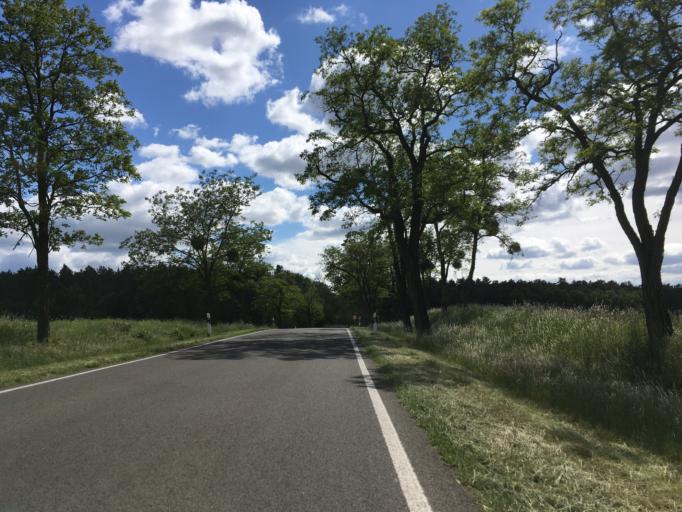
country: DE
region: Brandenburg
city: Protzel
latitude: 52.6652
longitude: 13.9899
